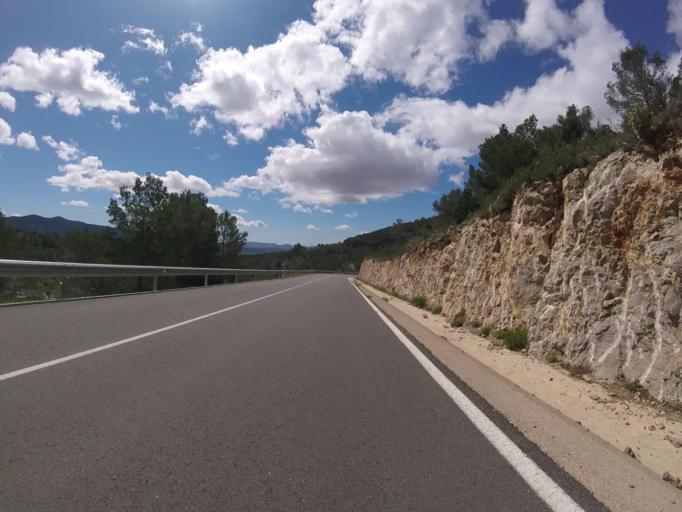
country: ES
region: Valencia
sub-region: Provincia de Castello
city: Adzaneta
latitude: 40.2732
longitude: -0.1100
